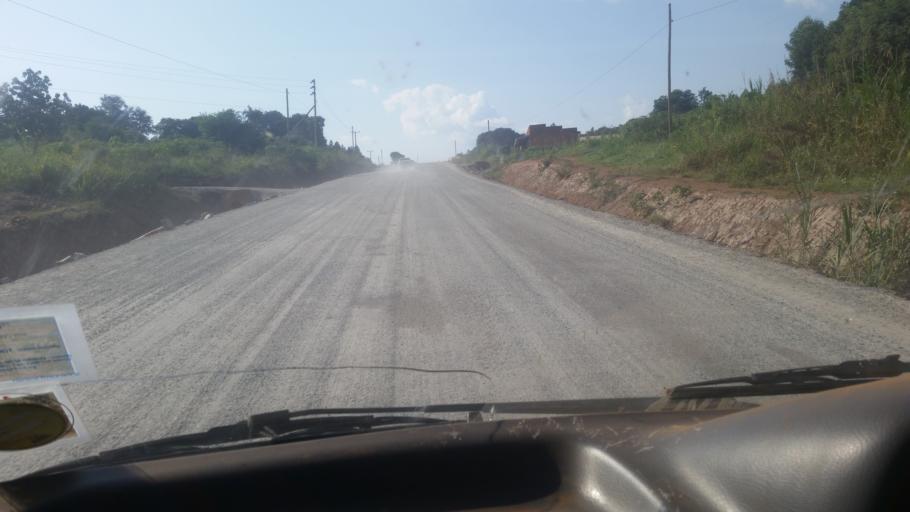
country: UG
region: Western Region
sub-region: Hoima District
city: Hoima
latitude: 1.3916
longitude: 31.3320
